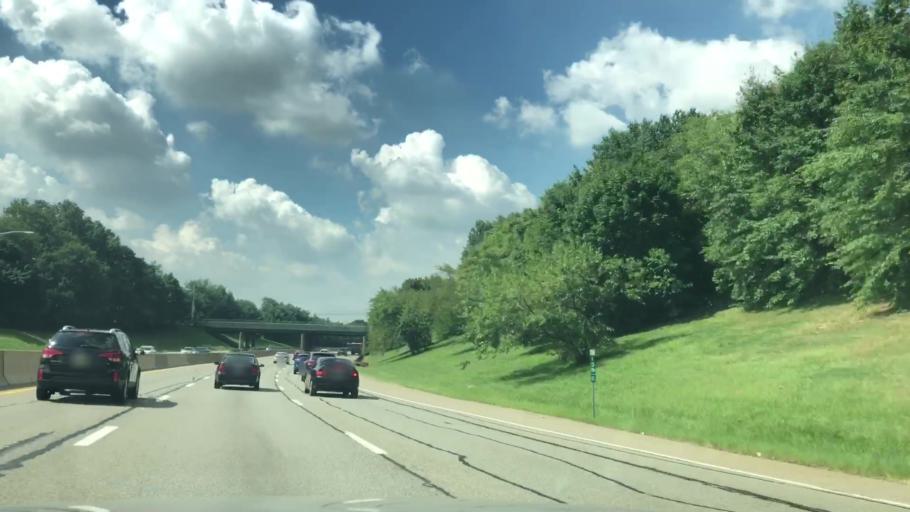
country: US
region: New Jersey
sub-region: Bergen County
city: Elmwood Park
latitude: 40.8919
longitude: -74.1225
